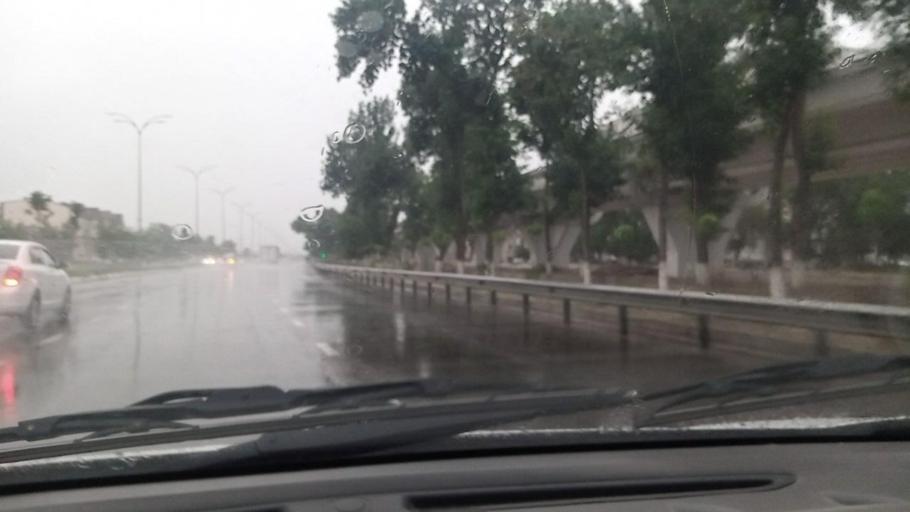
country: UZ
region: Toshkent Shahri
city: Bektemir
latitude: 41.2884
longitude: 69.3595
